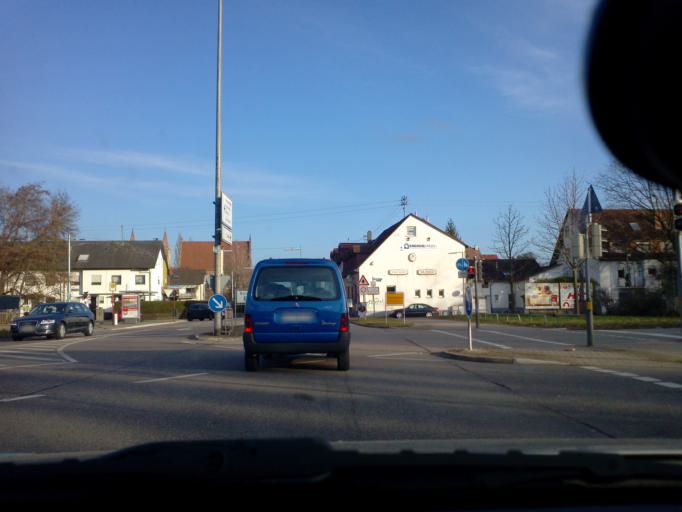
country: DE
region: Baden-Wuerttemberg
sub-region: Karlsruhe Region
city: Karlsruhe
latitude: 48.9891
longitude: 8.3761
